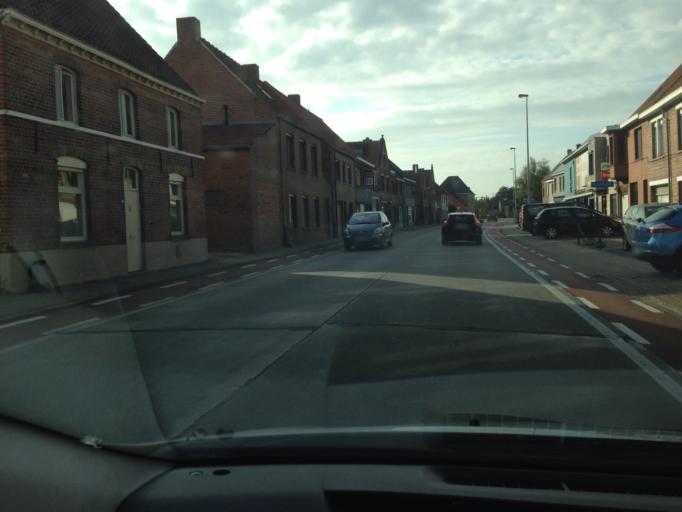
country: BE
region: Flanders
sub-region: Provincie West-Vlaanderen
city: Zedelgem
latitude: 51.1251
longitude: 3.1653
